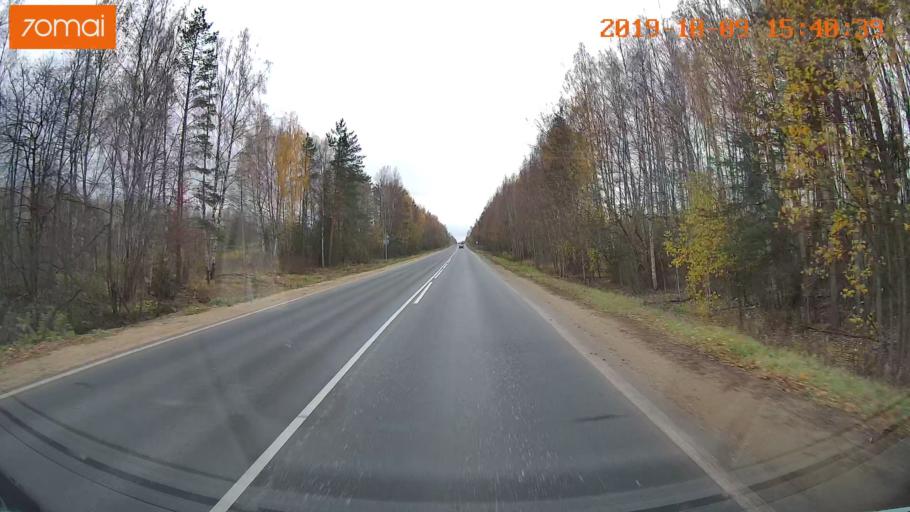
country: RU
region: Kostroma
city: Oktyabr'skiy
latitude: 57.8855
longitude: 41.1401
